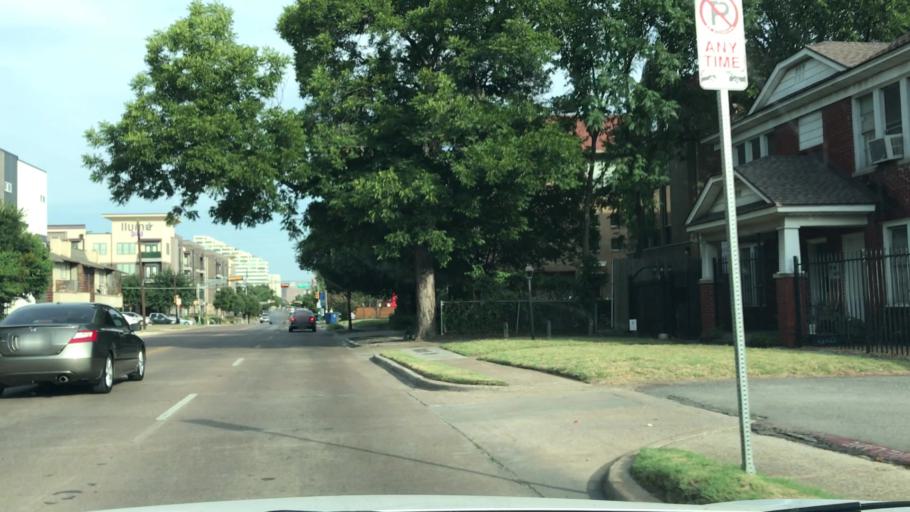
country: US
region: Texas
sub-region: Dallas County
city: Highland Park
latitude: 32.8146
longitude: -96.8159
